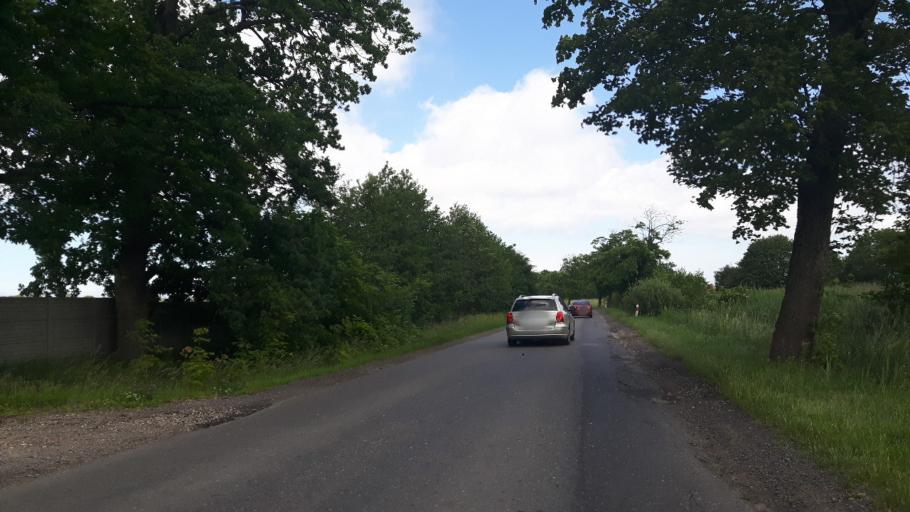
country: PL
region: Pomeranian Voivodeship
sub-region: Powiat slupski
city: Ustka
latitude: 54.5497
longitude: 16.8328
